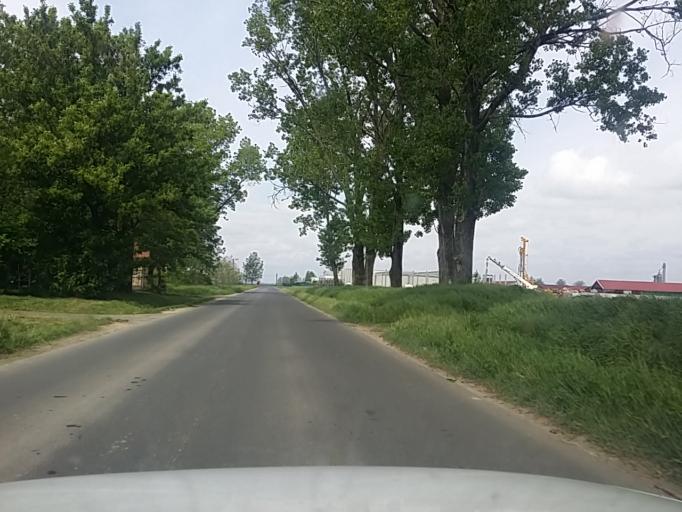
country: HU
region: Pest
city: Szentlorinckata
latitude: 47.5111
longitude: 19.7499
